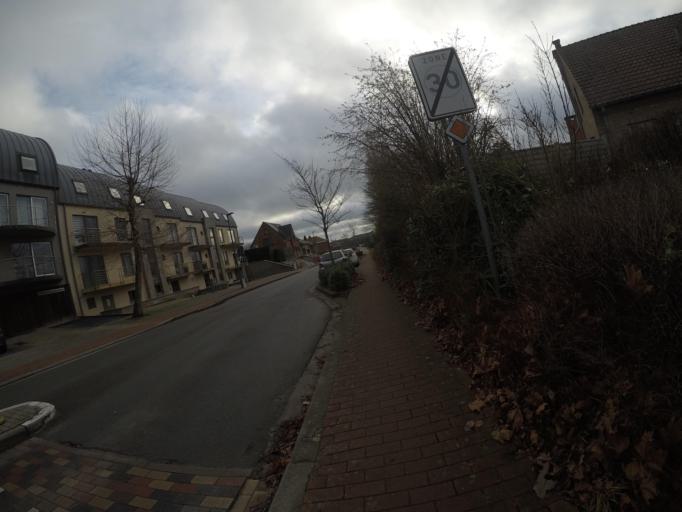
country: BE
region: Flanders
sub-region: Provincie Vlaams-Brabant
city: Ledeberg
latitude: 50.8406
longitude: 4.0805
